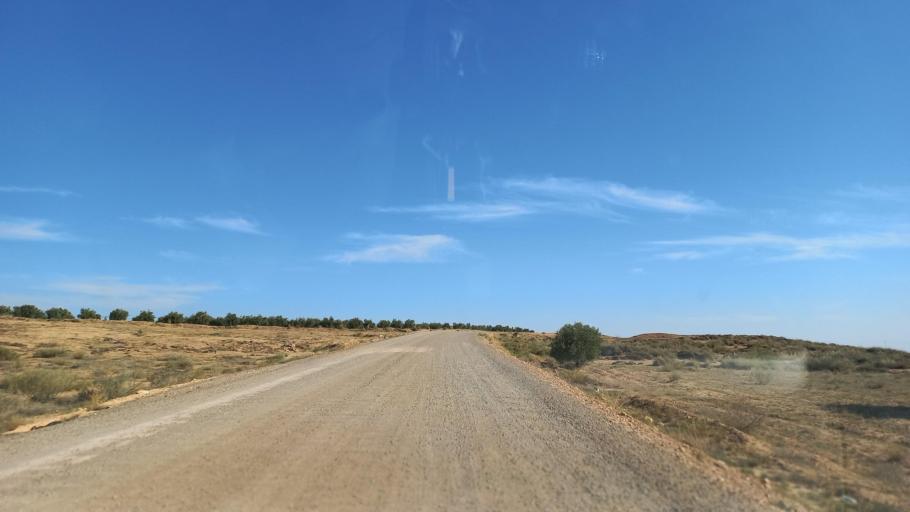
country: TN
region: Al Qasrayn
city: Sbiba
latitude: 35.3003
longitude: 9.0961
